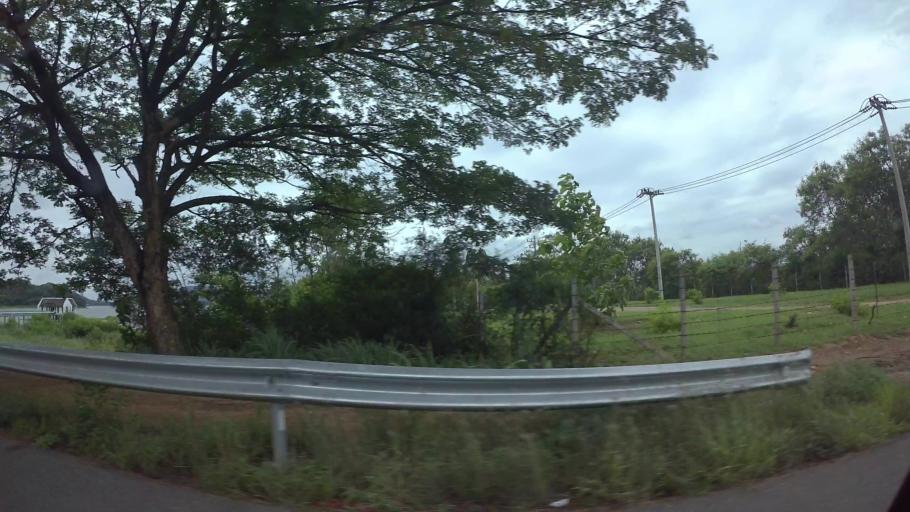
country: TH
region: Chon Buri
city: Si Racha
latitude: 13.1948
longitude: 100.9616
